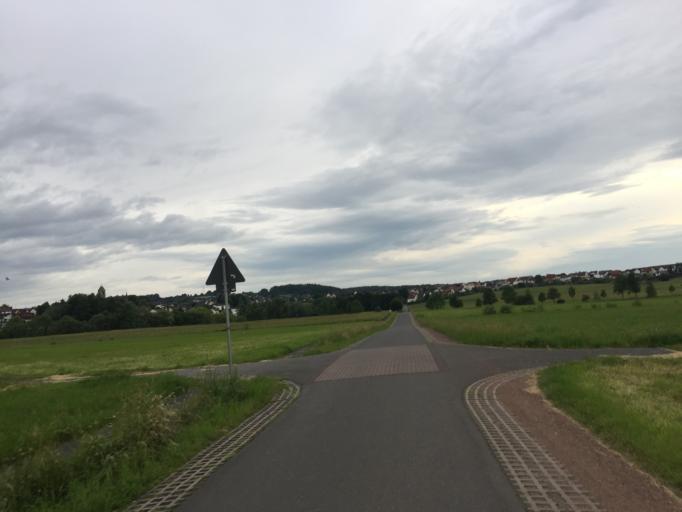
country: DE
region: Hesse
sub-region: Regierungsbezirk Giessen
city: Giessen
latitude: 50.5413
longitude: 8.7178
